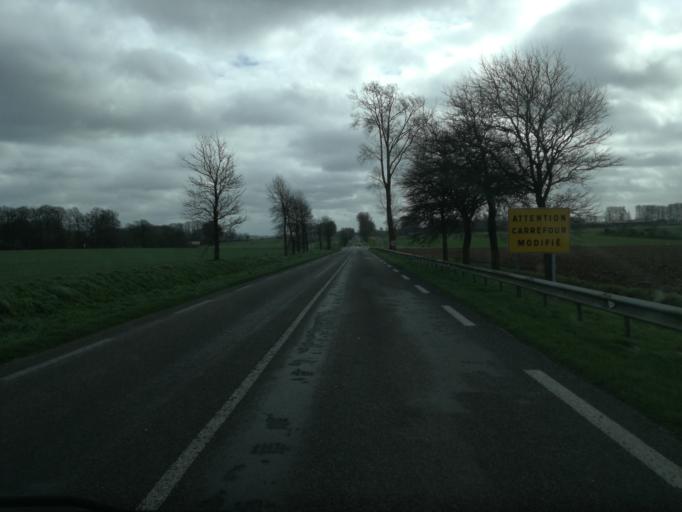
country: FR
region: Haute-Normandie
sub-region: Departement de la Seine-Maritime
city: Valliquerville
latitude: 49.6245
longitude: 0.6473
